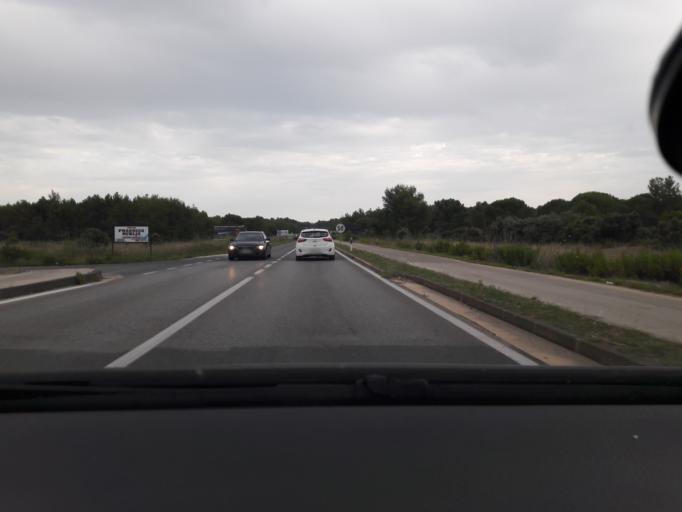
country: HR
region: Zadarska
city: Nin
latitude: 44.2131
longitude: 15.1783
